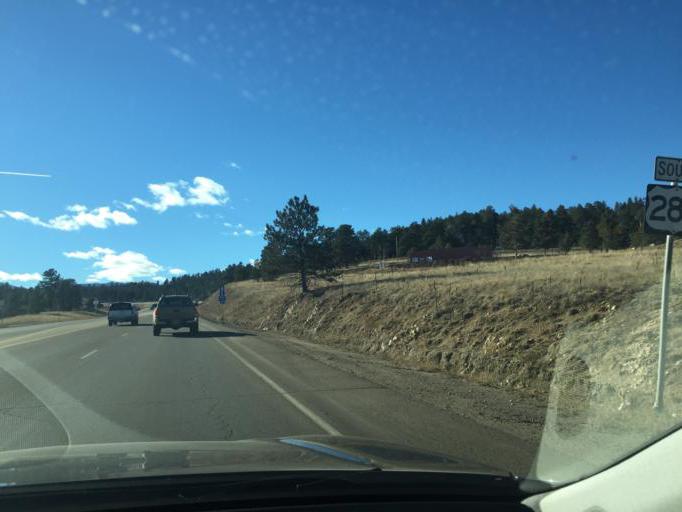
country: US
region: Colorado
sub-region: Jefferson County
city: Evergreen
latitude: 39.4390
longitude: -105.4542
